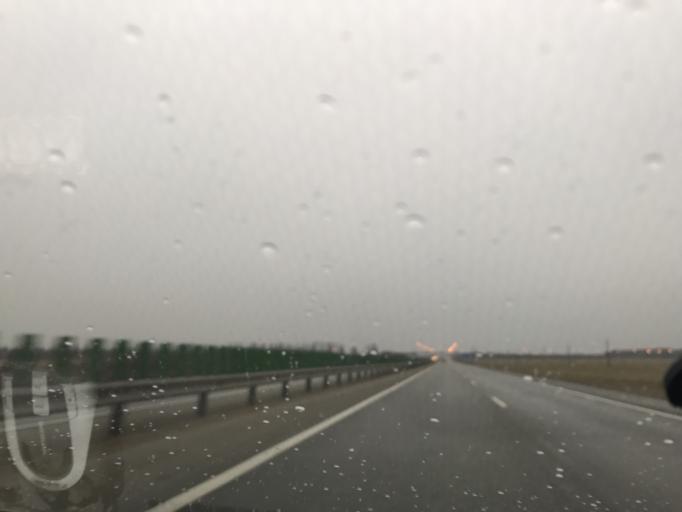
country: RU
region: Krasnodarskiy
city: Pavlovskaya
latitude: 46.2440
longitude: 39.8314
